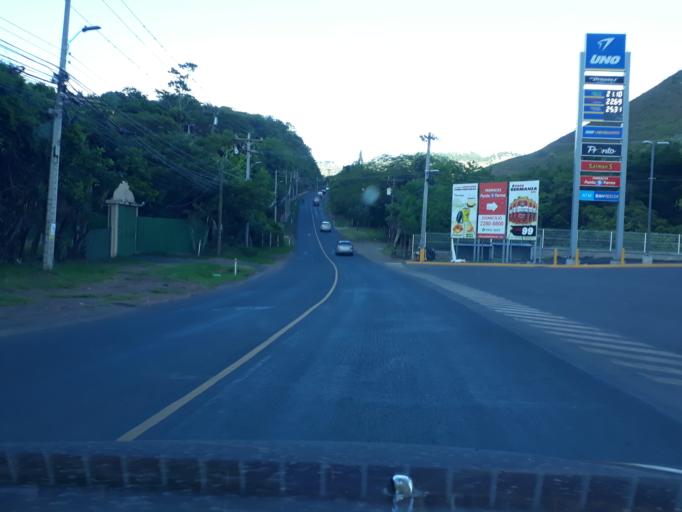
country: HN
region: Francisco Morazan
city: Santa Lucia
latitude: 14.1106
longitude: -87.1650
